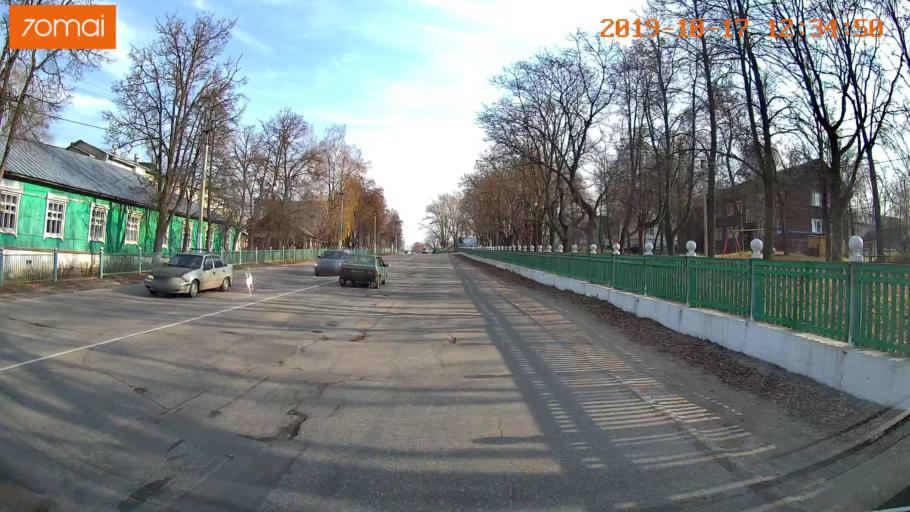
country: RU
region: Rjazan
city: Kasimov
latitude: 54.9459
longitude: 41.3681
